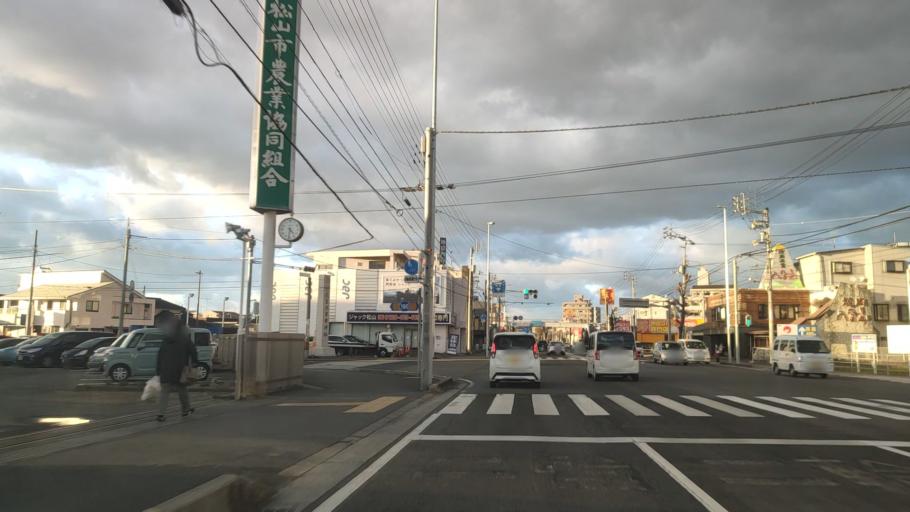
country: JP
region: Ehime
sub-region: Shikoku-chuo Shi
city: Matsuyama
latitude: 33.8089
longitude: 132.7802
